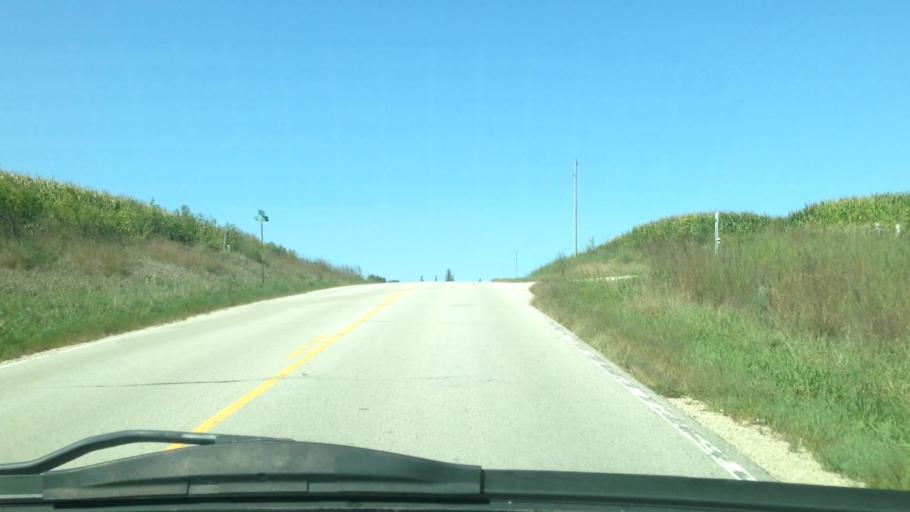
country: US
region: Minnesota
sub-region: Fillmore County
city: Rushford
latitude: 43.6984
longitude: -91.7703
